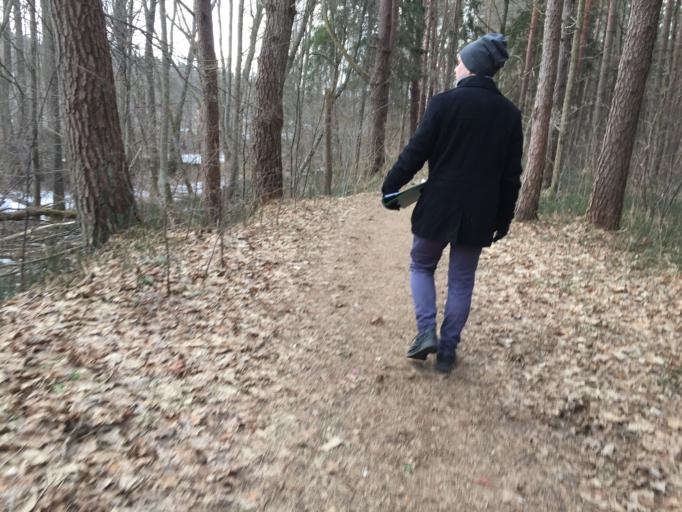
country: LV
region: Valmieras Rajons
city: Valmiera
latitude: 57.5350
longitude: 25.4422
